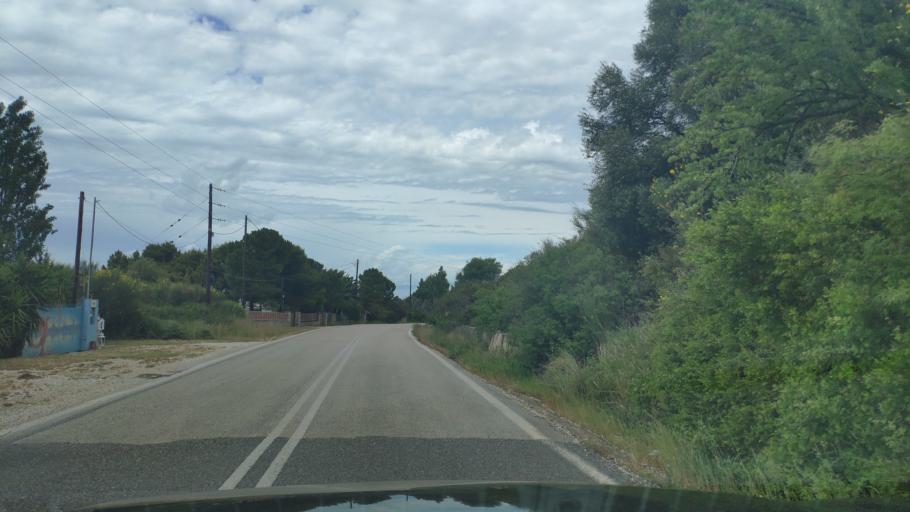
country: GR
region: West Greece
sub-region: Nomos Aitolias kai Akarnanias
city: Palairos
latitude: 38.7614
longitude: 20.8826
